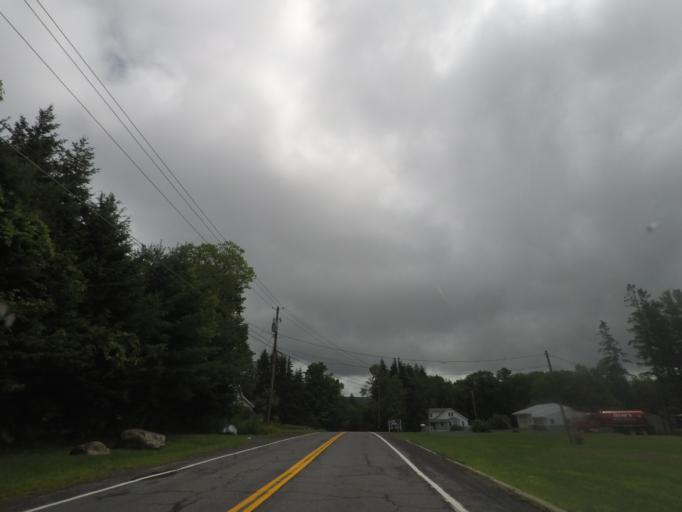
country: US
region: New York
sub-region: Rensselaer County
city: Averill Park
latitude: 42.5913
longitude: -73.4990
